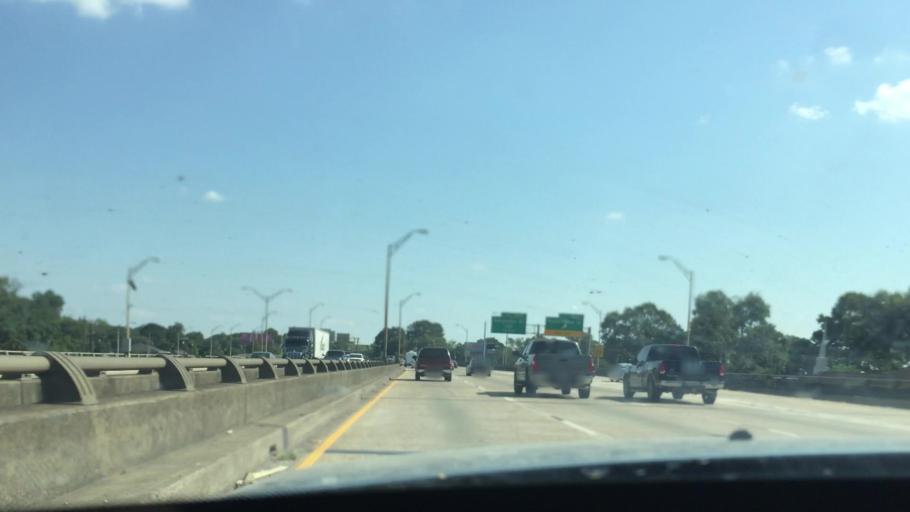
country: US
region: Louisiana
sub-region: East Baton Rouge Parish
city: Baton Rouge
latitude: 30.4340
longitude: -91.1767
